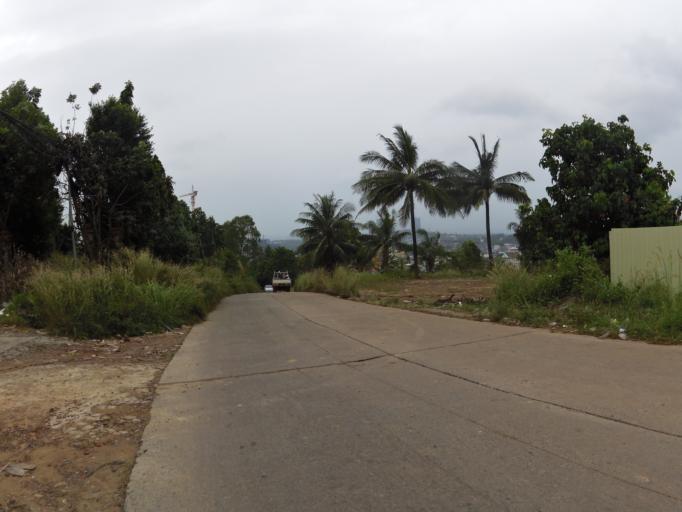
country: KH
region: Preah Sihanouk
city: Sihanoukville
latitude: 10.6284
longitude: 103.5265
